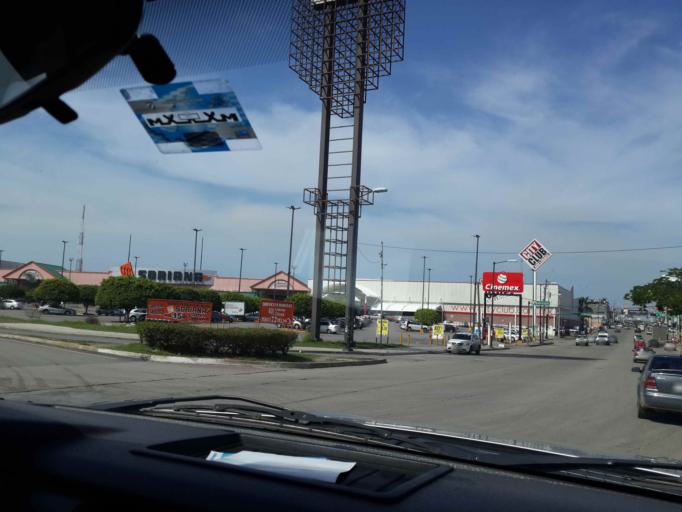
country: MX
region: Tamaulipas
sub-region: Tampico
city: Tampico
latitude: 22.2509
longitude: -97.8626
